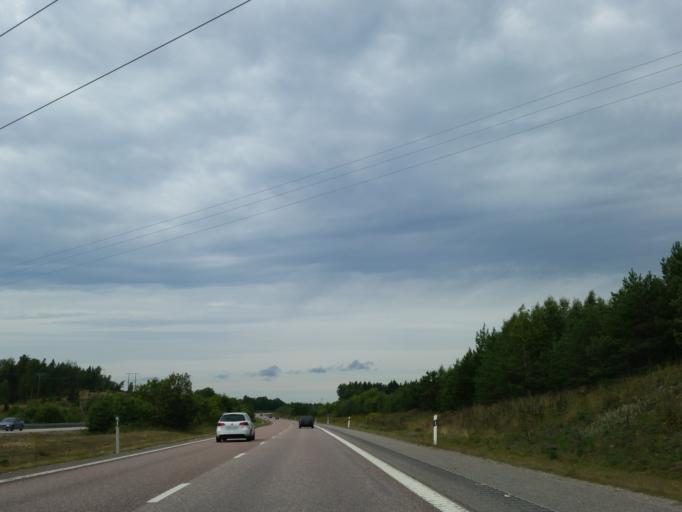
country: SE
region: Stockholm
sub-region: Nykvarns Kommun
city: Nykvarn
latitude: 59.2034
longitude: 17.3593
